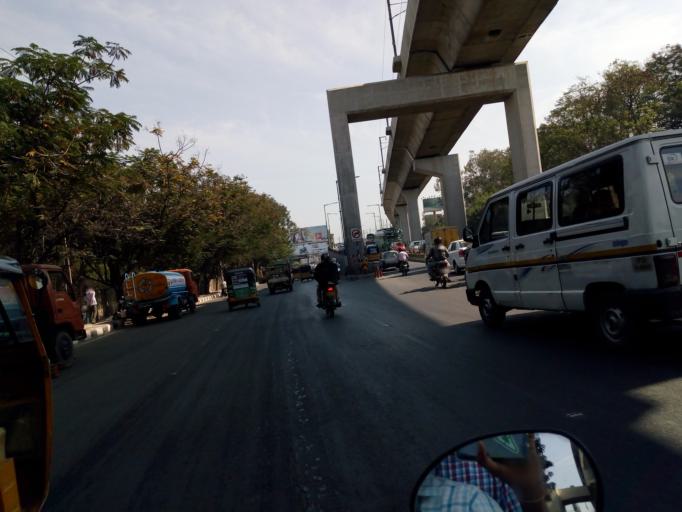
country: IN
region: Telangana
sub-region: Hyderabad
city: Malkajgiri
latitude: 17.4280
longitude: 78.5295
